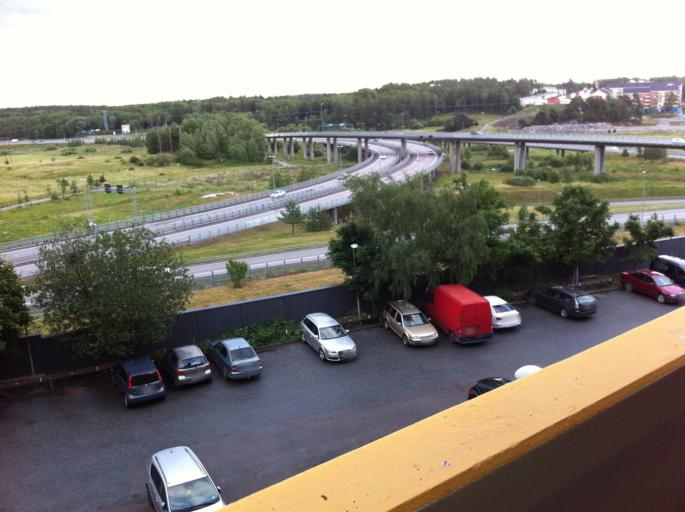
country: SE
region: Stockholm
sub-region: Stockholms Kommun
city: Kista
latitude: 59.3880
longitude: 17.9276
